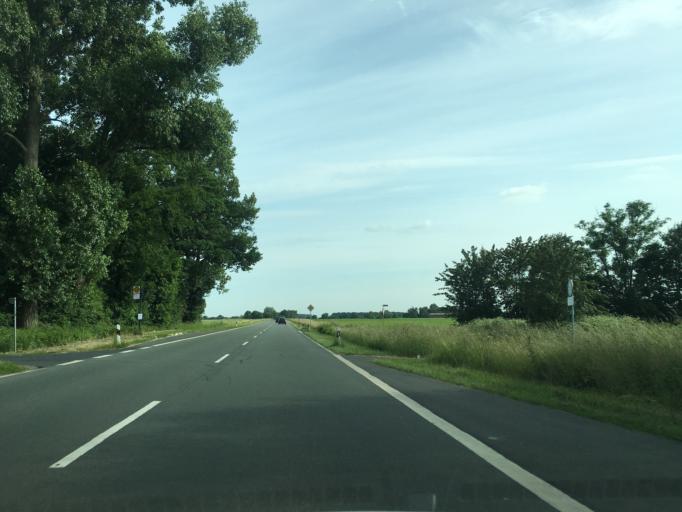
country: DE
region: North Rhine-Westphalia
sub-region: Regierungsbezirk Munster
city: Senden
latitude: 51.8382
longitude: 7.4895
